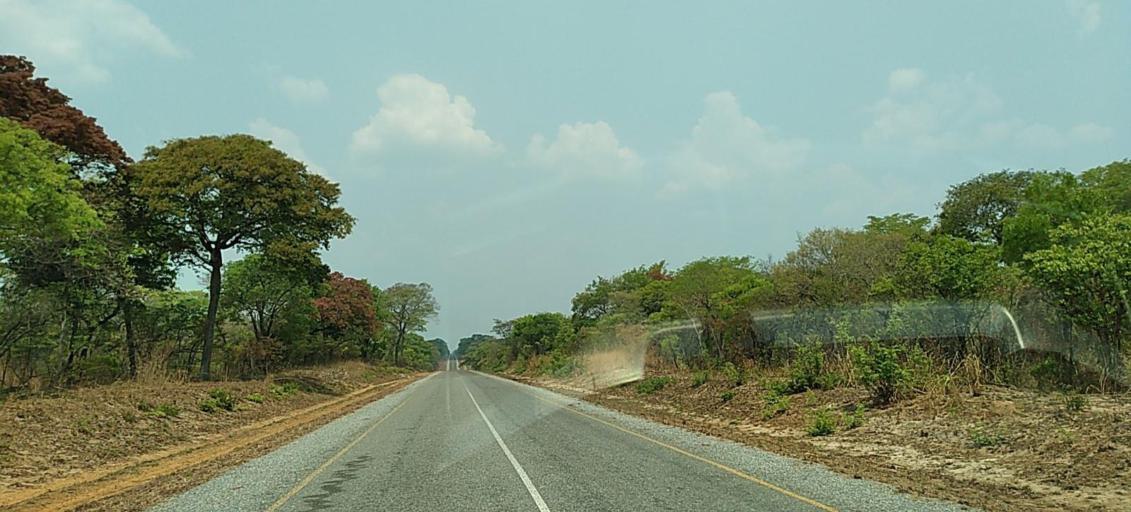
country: ZM
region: North-Western
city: Zambezi
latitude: -13.5654
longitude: 23.2211
